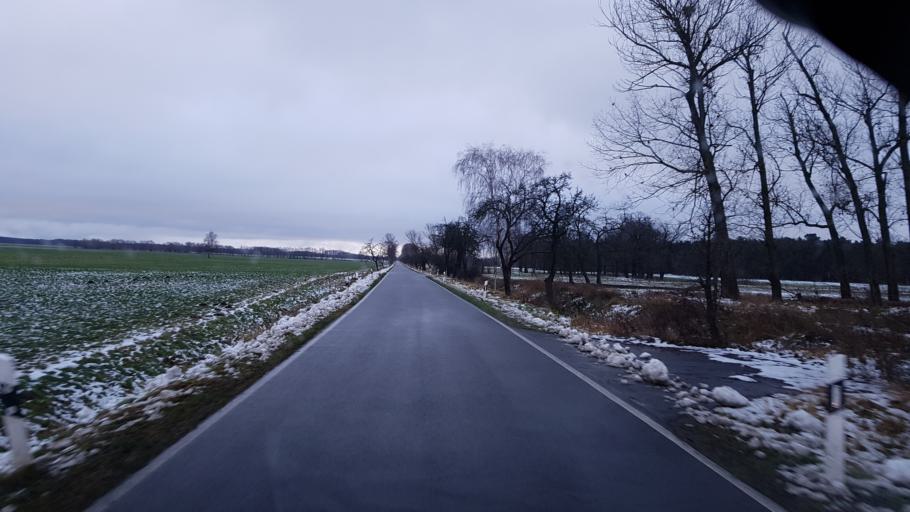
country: DE
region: Brandenburg
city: Luckau
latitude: 51.8160
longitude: 13.7013
